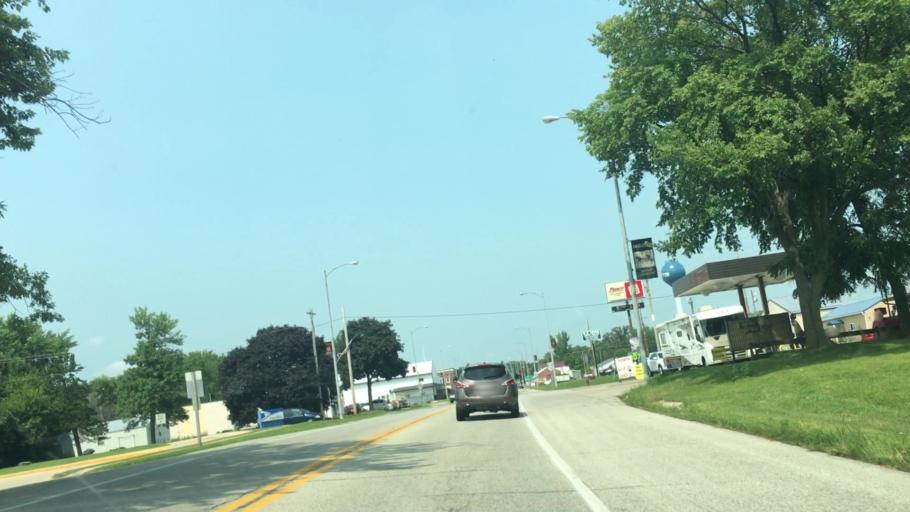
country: US
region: Iowa
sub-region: Fayette County
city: Oelwein
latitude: 42.6149
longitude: -91.9055
